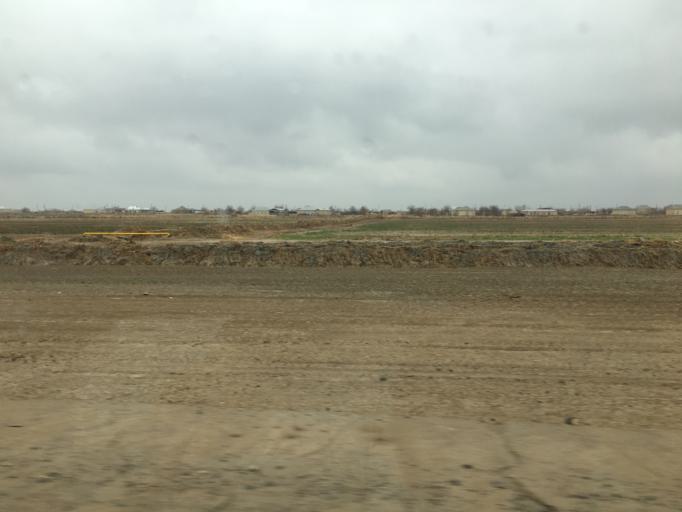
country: TM
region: Mary
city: Yoloeten
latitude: 37.4018
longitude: 62.1757
